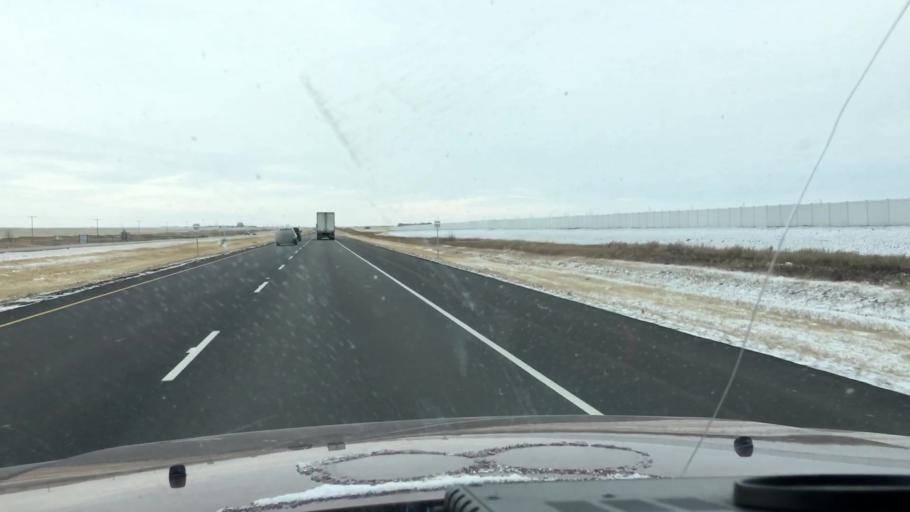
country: CA
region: Saskatchewan
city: Saskatoon
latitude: 51.8064
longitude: -106.4933
